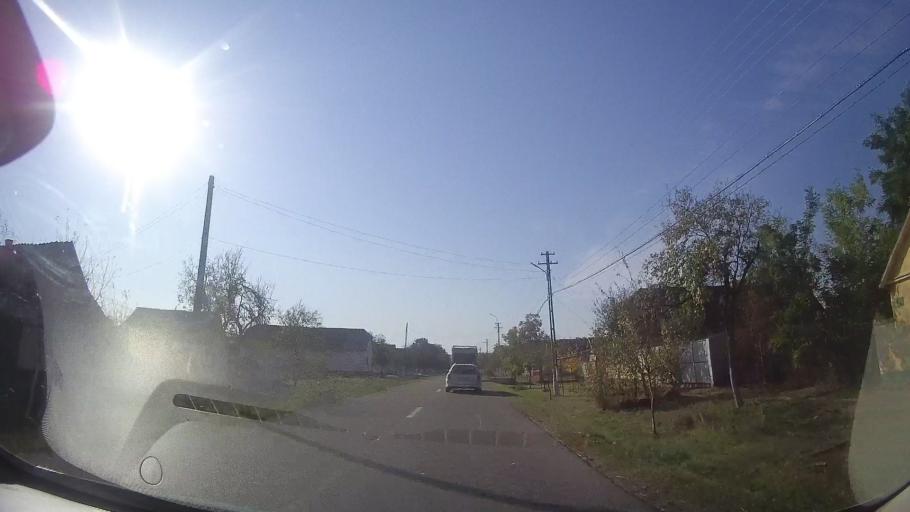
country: RO
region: Timis
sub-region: Oras Recas
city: Recas
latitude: 45.8541
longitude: 21.5160
